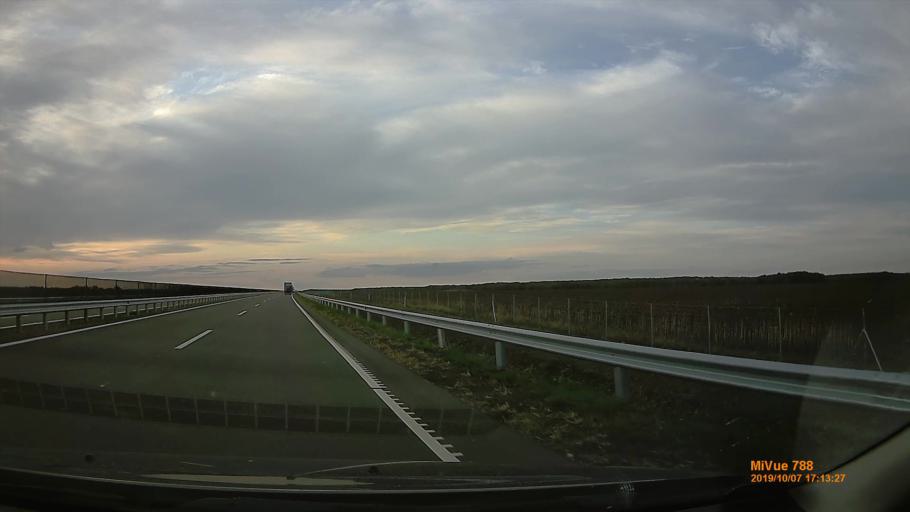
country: HU
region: Jasz-Nagykun-Szolnok
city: Kunszentmarton
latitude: 46.8209
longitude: 20.3708
